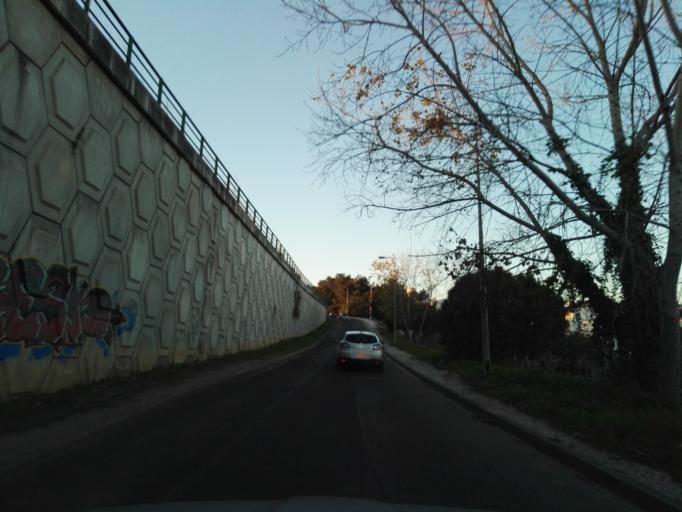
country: PT
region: Setubal
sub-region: Seixal
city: Corroios
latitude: 38.6426
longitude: -9.1489
